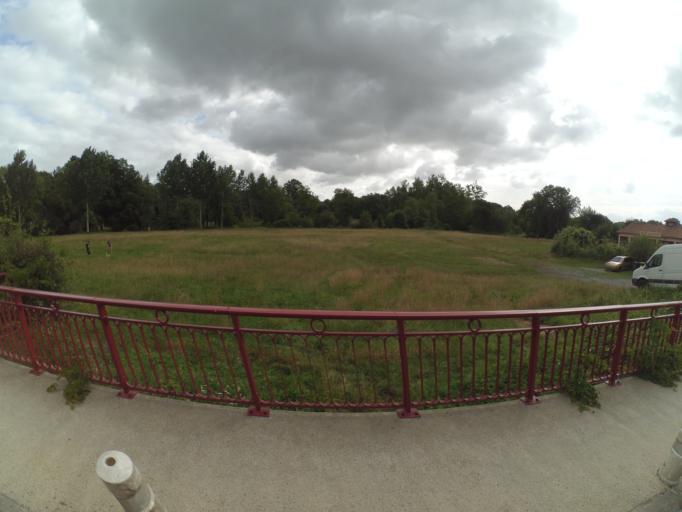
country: FR
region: Pays de la Loire
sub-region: Departement de Maine-et-Loire
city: Montfaucon-Montigne
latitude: 47.0977
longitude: -1.1262
